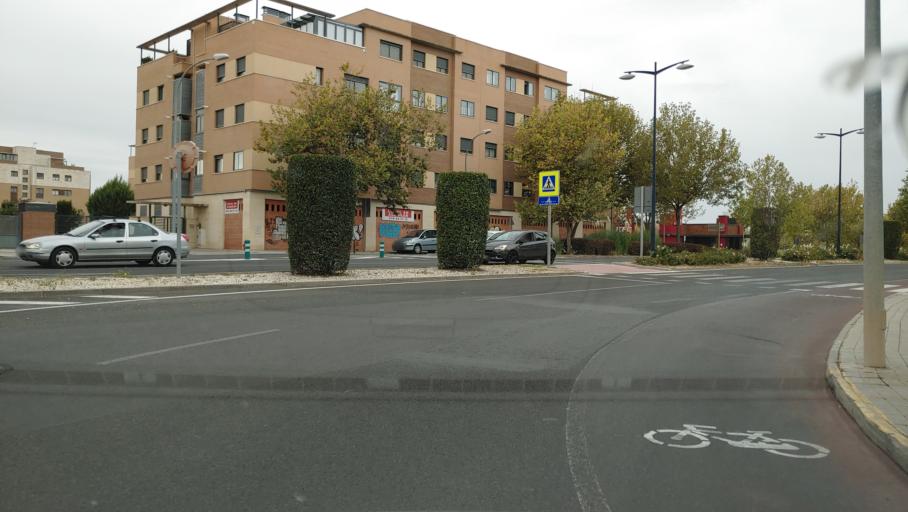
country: ES
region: Castille-La Mancha
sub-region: Provincia de Ciudad Real
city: Ciudad Real
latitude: 38.9731
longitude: -3.9360
